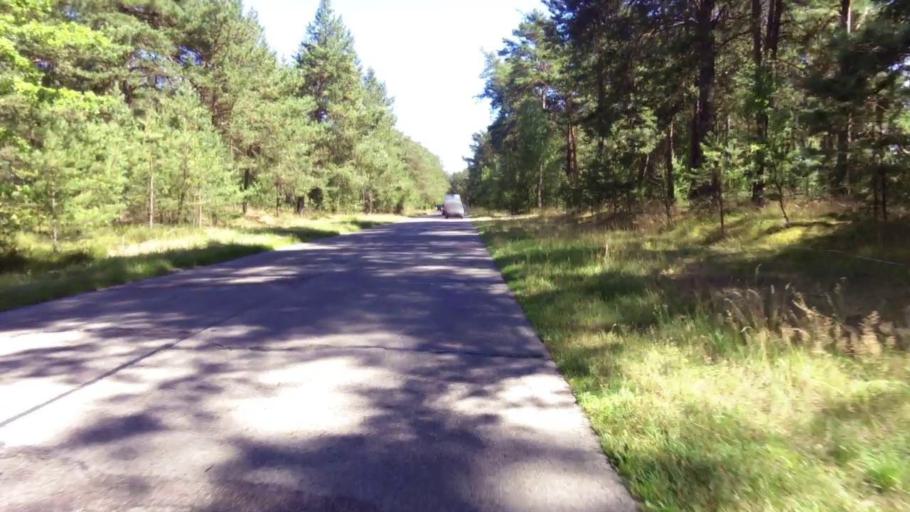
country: PL
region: West Pomeranian Voivodeship
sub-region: Powiat szczecinecki
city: Borne Sulinowo
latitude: 53.5858
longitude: 16.5031
